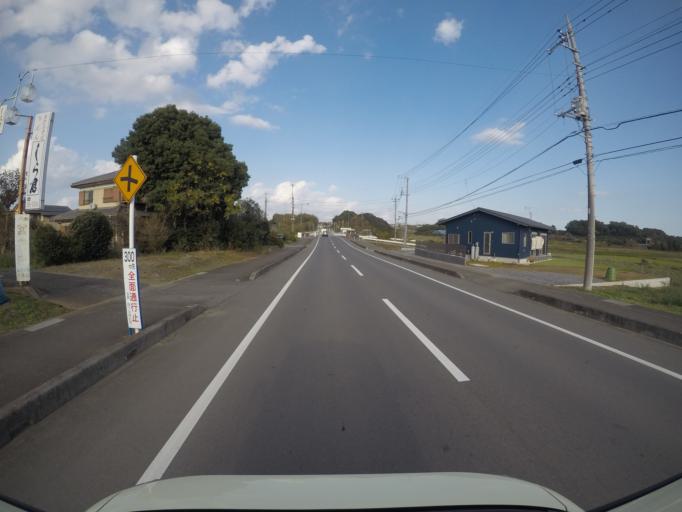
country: JP
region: Ibaraki
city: Ushiku
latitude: 36.0295
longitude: 140.0805
